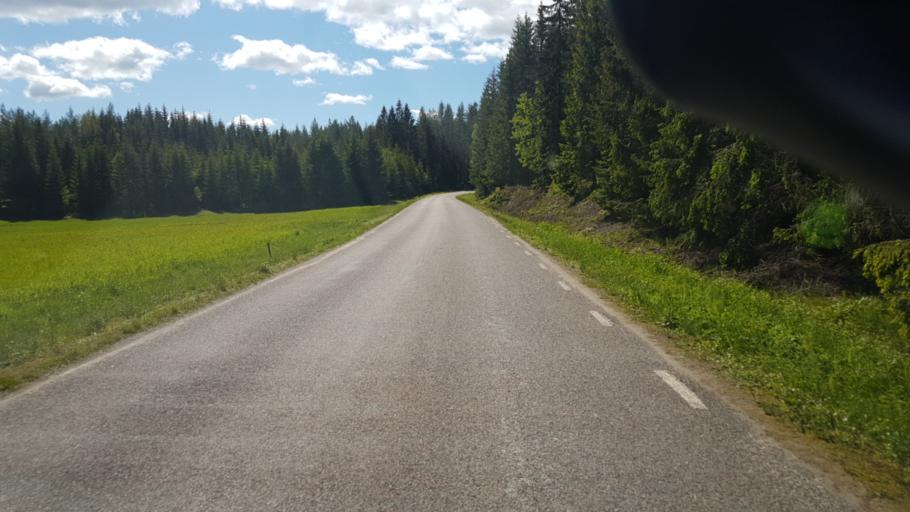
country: SE
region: Vaermland
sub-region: Grums Kommun
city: Grums
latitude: 59.4971
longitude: 12.8777
